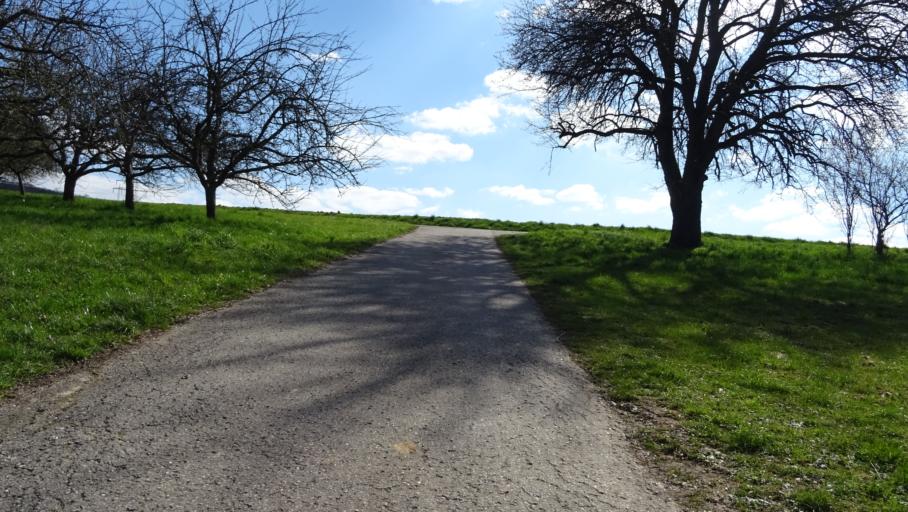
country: DE
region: Baden-Wuerttemberg
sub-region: Karlsruhe Region
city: Neckarzimmern
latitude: 49.3322
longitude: 9.1148
